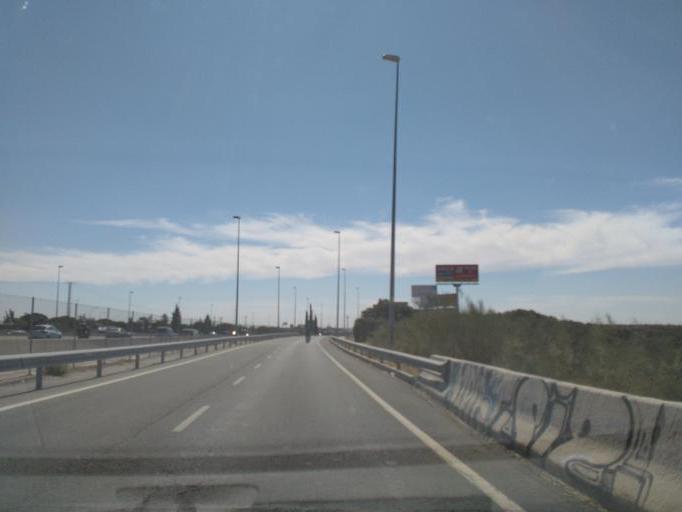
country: ES
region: Madrid
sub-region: Provincia de Madrid
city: Las Matas
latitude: 40.5612
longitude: -3.9032
